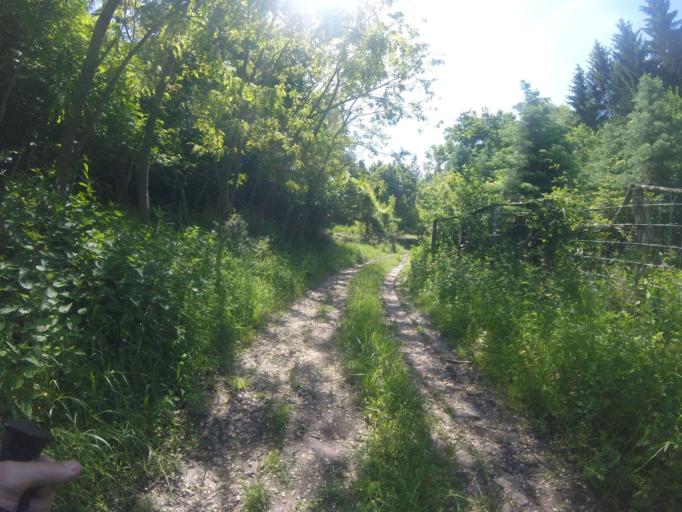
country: HU
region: Nograd
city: Matraverebely
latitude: 47.9404
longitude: 19.7956
